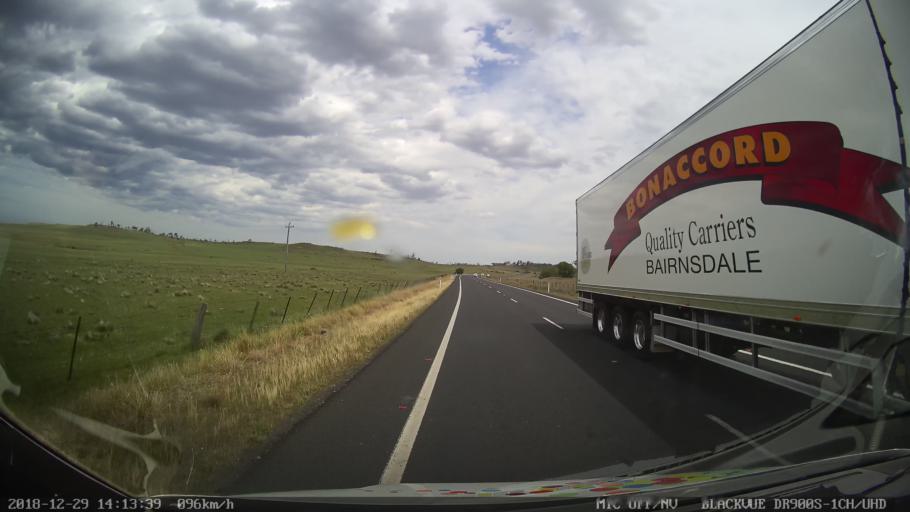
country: AU
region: New South Wales
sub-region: Cooma-Monaro
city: Cooma
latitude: -36.4311
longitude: 149.2383
